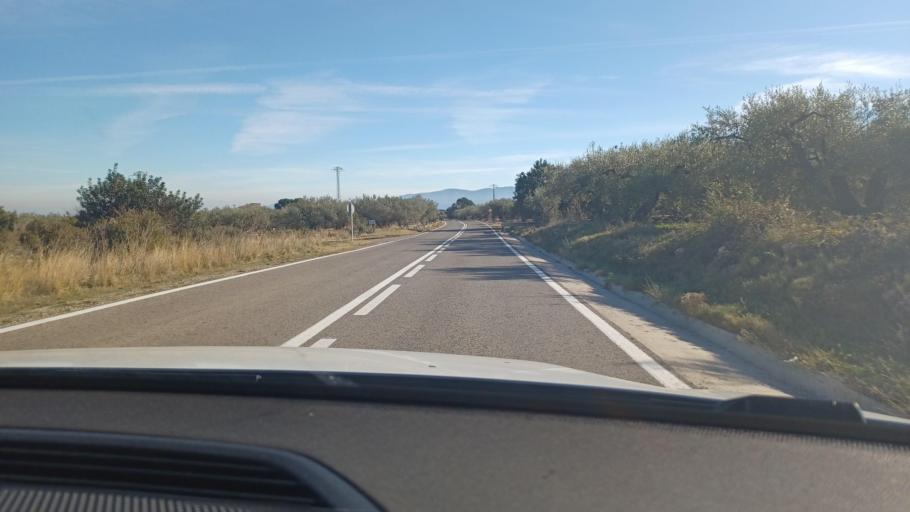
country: ES
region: Catalonia
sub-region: Provincia de Tarragona
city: Mas de Barberans
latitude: 40.7290
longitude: 0.3803
